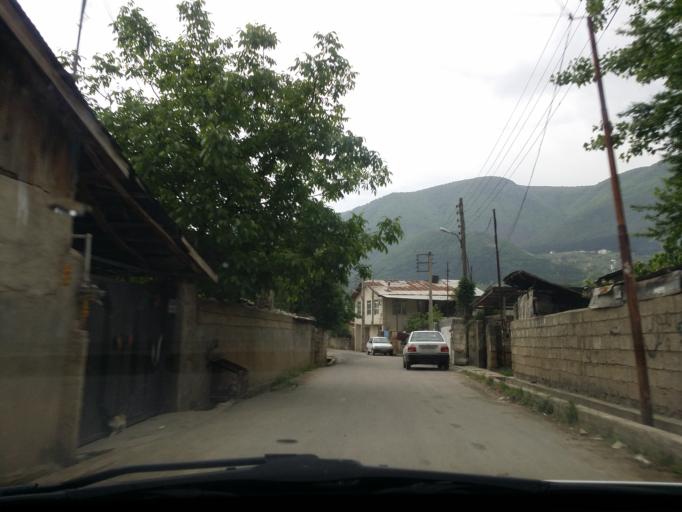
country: IR
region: Mazandaran
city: `Abbasabad
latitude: 36.5036
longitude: 51.1477
